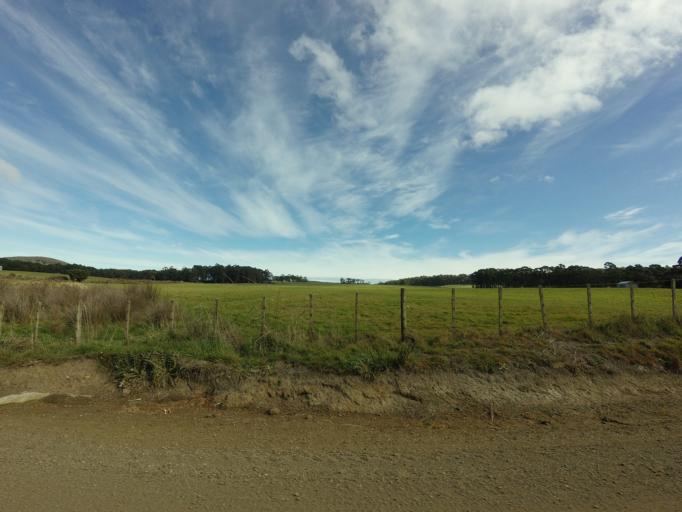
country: AU
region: Tasmania
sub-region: Clarence
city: Sandford
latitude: -43.1578
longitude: 147.7669
